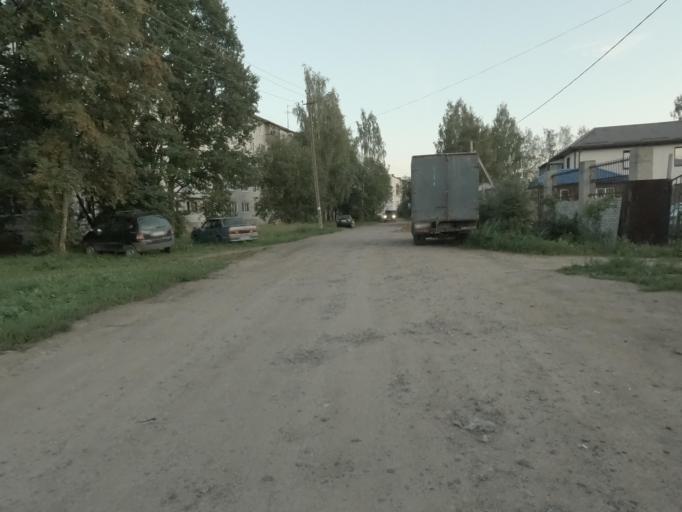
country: RU
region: Leningrad
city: Mga
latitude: 59.7602
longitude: 31.0544
